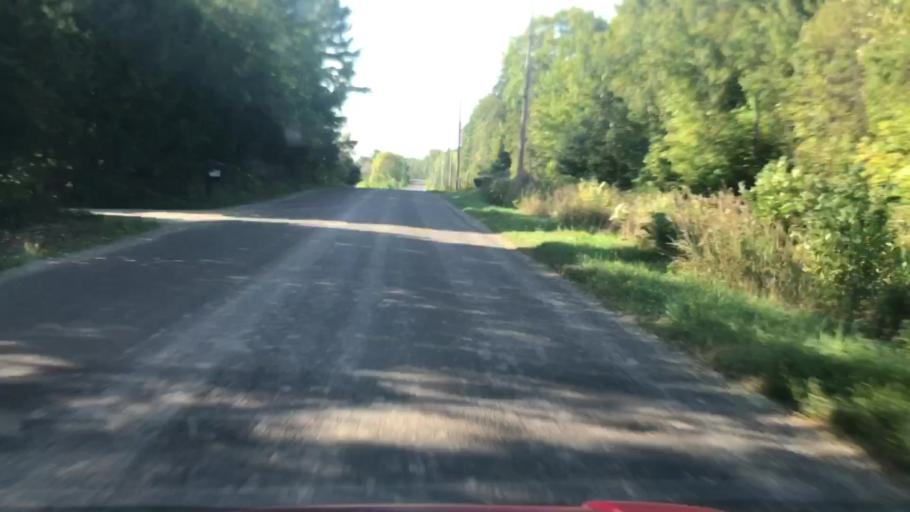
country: US
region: Michigan
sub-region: Chippewa County
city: Sault Ste. Marie
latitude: 46.2889
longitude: -84.0616
